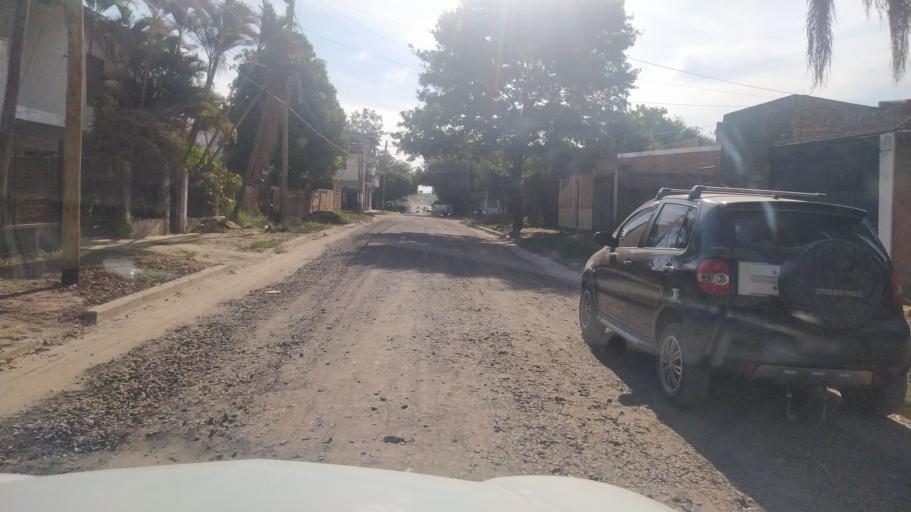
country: AR
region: Corrientes
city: Corrientes
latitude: -27.4878
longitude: -58.8142
